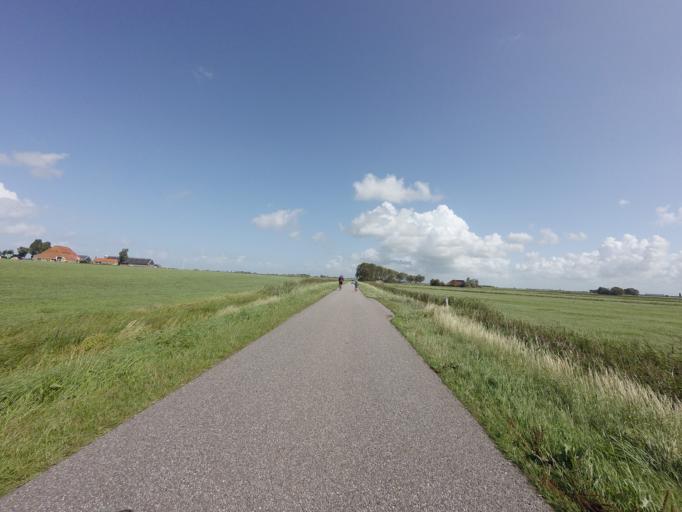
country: NL
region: Friesland
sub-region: Sudwest Fryslan
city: Makkum
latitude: 53.0627
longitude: 5.4357
